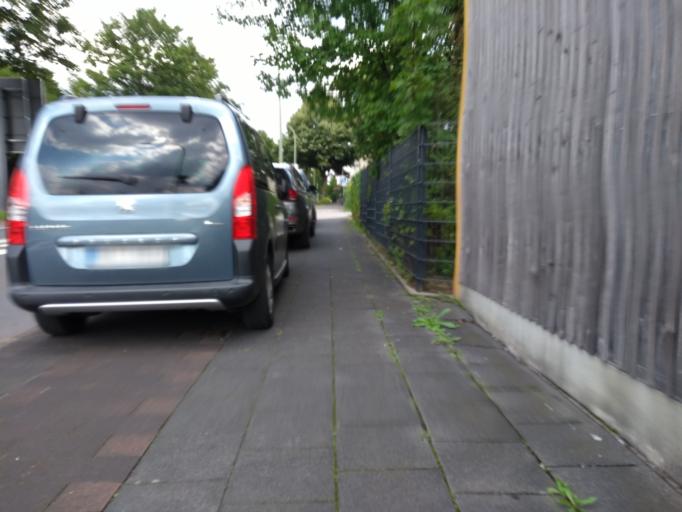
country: DE
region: North Rhine-Westphalia
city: Herdecke
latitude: 51.3923
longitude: 7.4665
